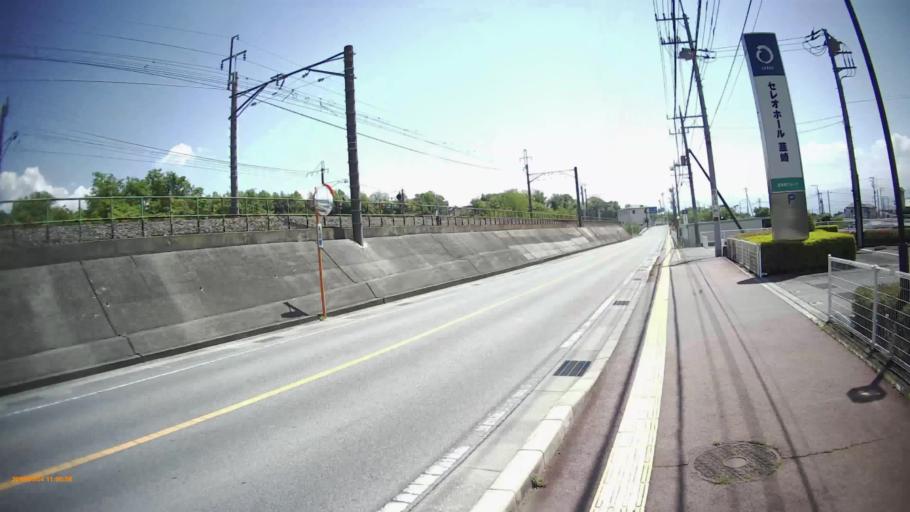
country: JP
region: Yamanashi
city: Nirasaki
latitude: 35.6993
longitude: 138.4640
